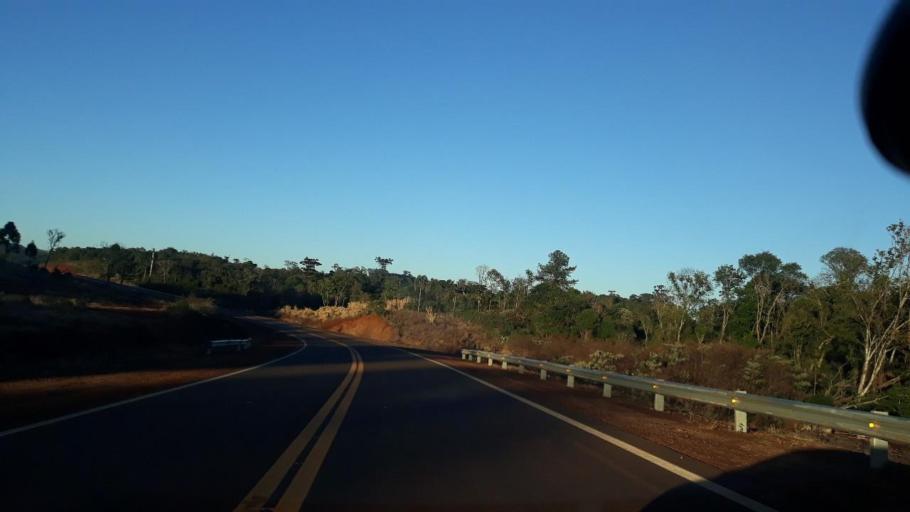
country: AR
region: Misiones
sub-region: Departamento de San Pedro
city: San Pedro
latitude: -26.5386
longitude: -53.9587
